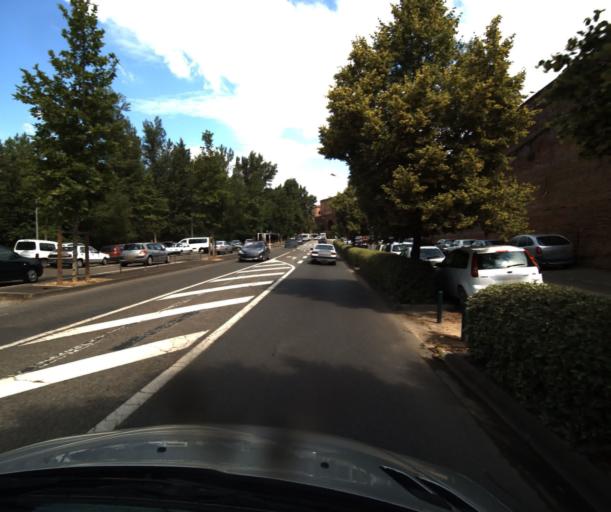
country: FR
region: Midi-Pyrenees
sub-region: Departement du Tarn-et-Garonne
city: Montauban
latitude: 44.0176
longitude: 1.3511
